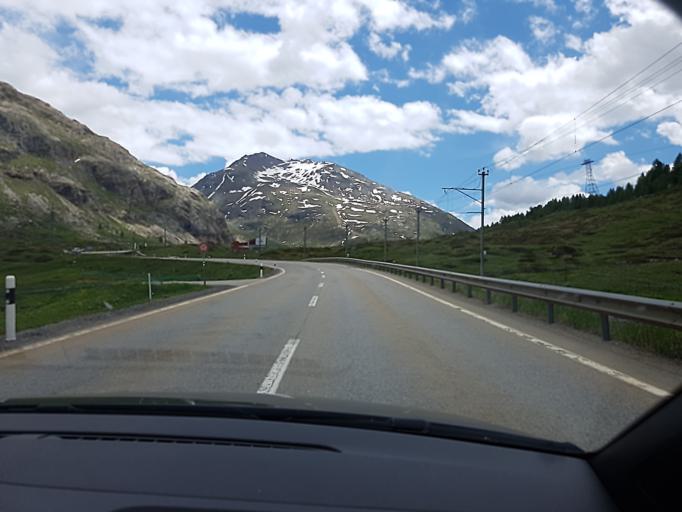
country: CH
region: Grisons
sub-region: Maloja District
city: Pontresina
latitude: 46.4430
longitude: 9.9749
